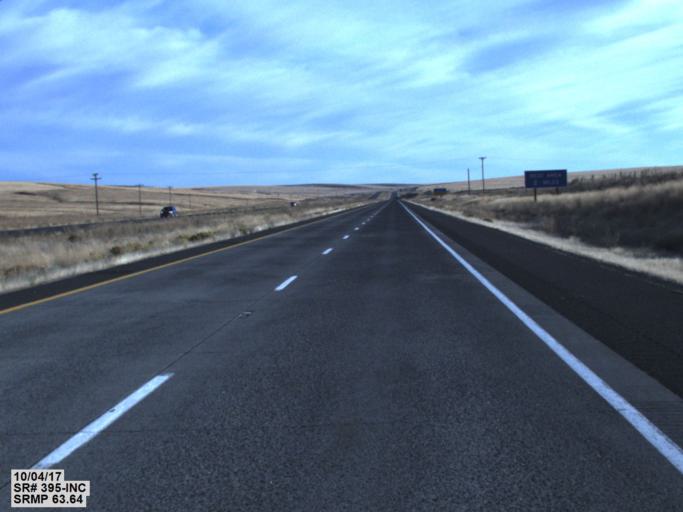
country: US
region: Washington
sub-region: Franklin County
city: Connell
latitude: 46.7626
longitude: -118.7878
